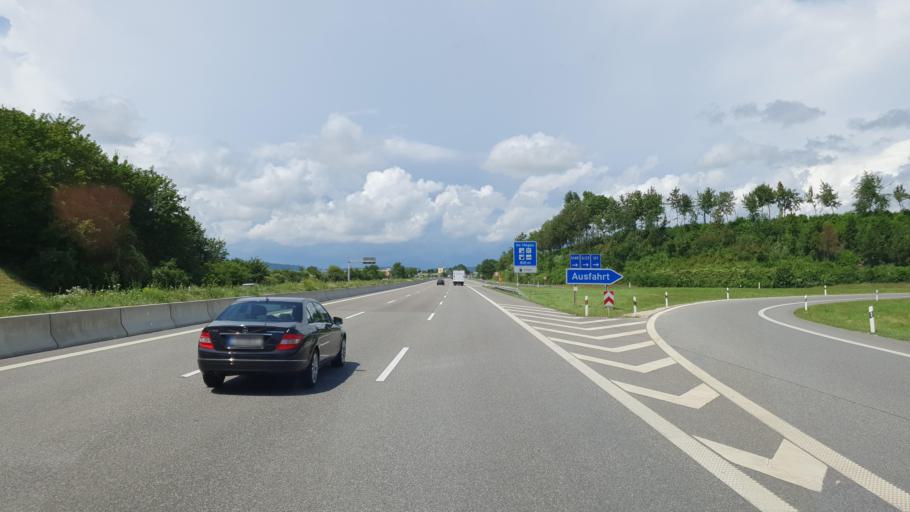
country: DE
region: Baden-Wuerttemberg
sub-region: Freiburg Region
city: Engen
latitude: 47.8547
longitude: 8.7989
